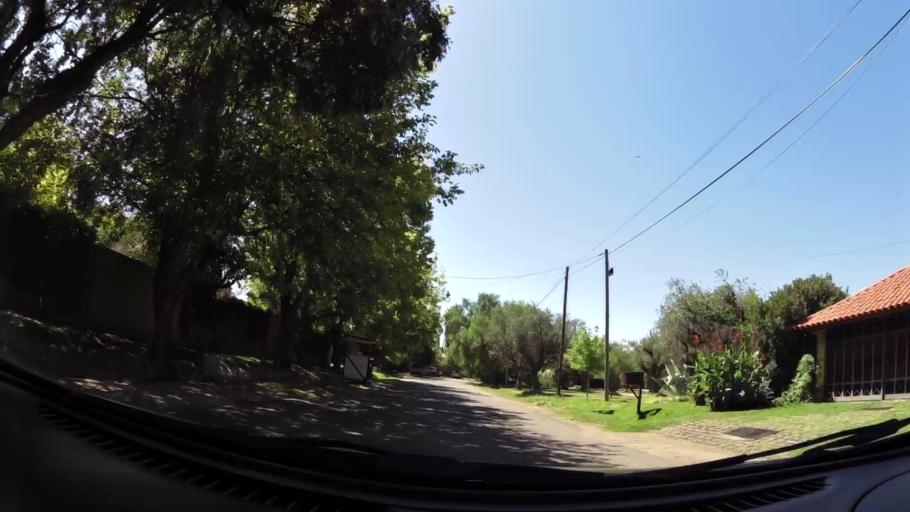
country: AR
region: Mendoza
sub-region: Departamento de Godoy Cruz
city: Godoy Cruz
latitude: -32.9697
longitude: -68.8720
